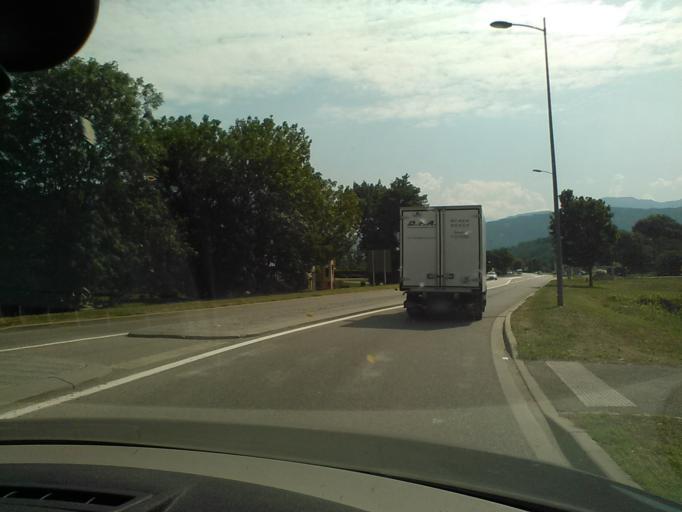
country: FR
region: Rhone-Alpes
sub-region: Departement de la Savoie
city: Montmelian
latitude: 45.4973
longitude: 6.0465
